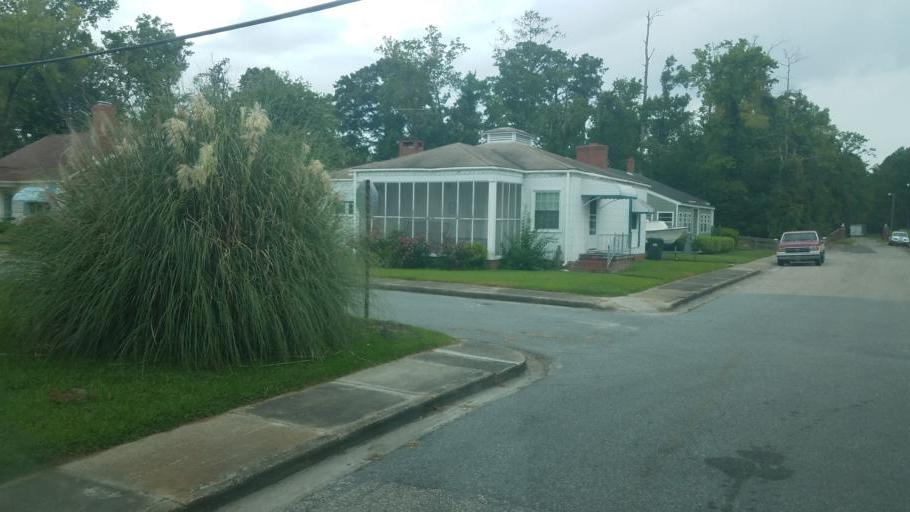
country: US
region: North Carolina
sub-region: Tyrrell County
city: Columbia
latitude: 35.9192
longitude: -76.2527
